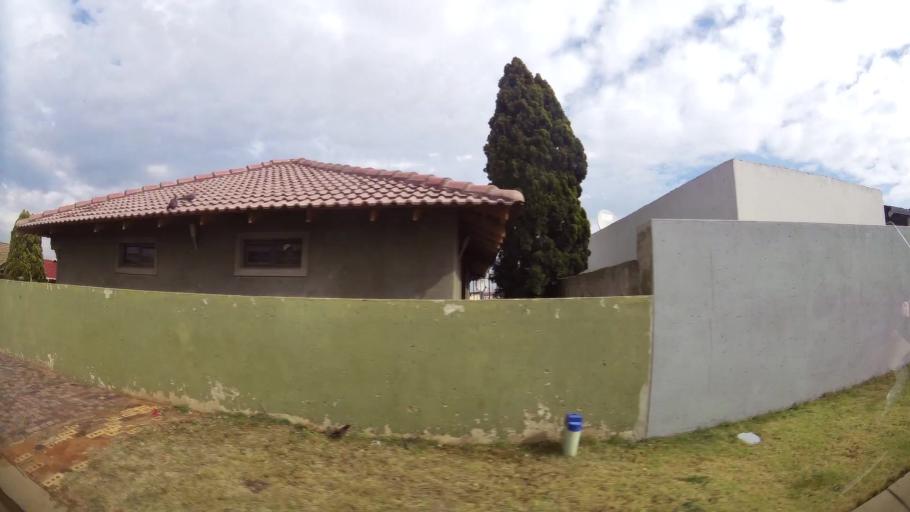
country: ZA
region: Gauteng
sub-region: Ekurhuleni Metropolitan Municipality
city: Germiston
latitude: -26.3219
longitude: 28.1770
